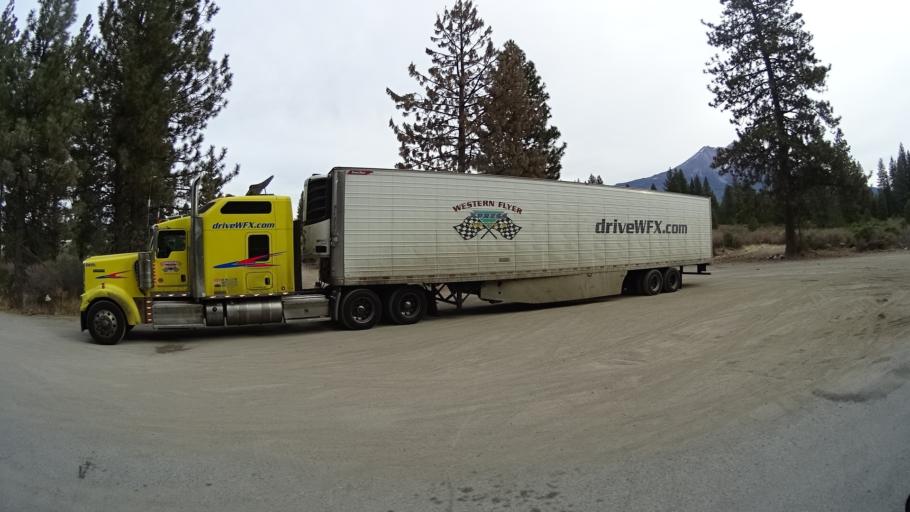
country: US
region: California
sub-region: Siskiyou County
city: Weed
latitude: 41.3964
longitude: -122.3756
